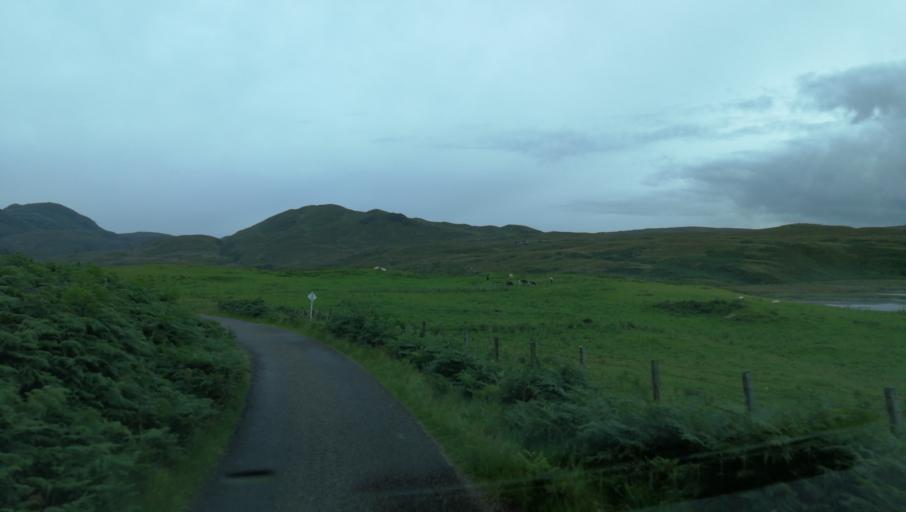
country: GB
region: Scotland
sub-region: Argyll and Bute
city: Isle Of Mull
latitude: 56.7232
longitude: -6.1953
